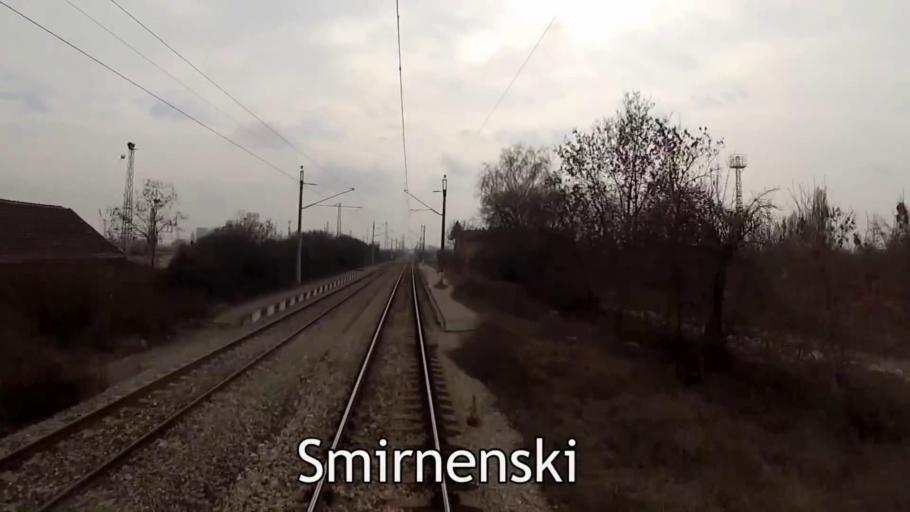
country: BG
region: Sofia-Capital
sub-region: Stolichna Obshtina
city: Sofia
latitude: 42.6701
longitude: 23.4026
